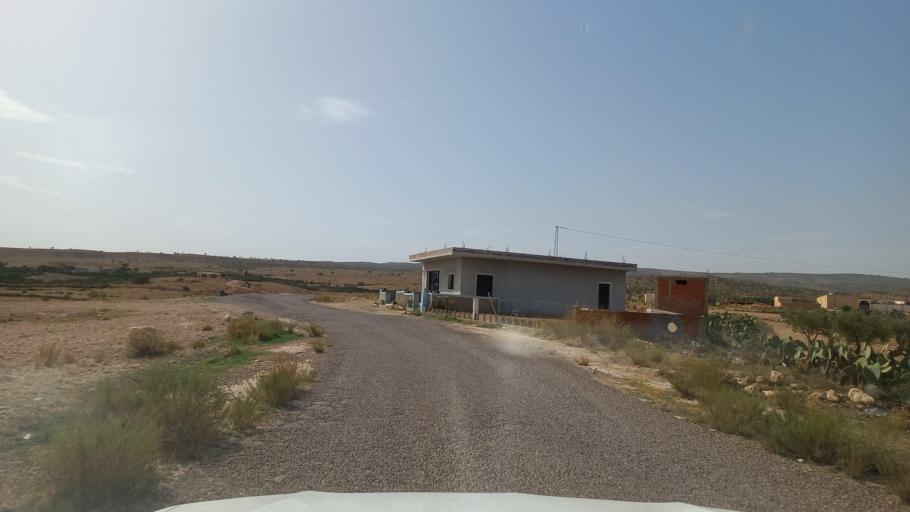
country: TN
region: Al Qasrayn
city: Kasserine
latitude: 35.3033
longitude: 8.9439
